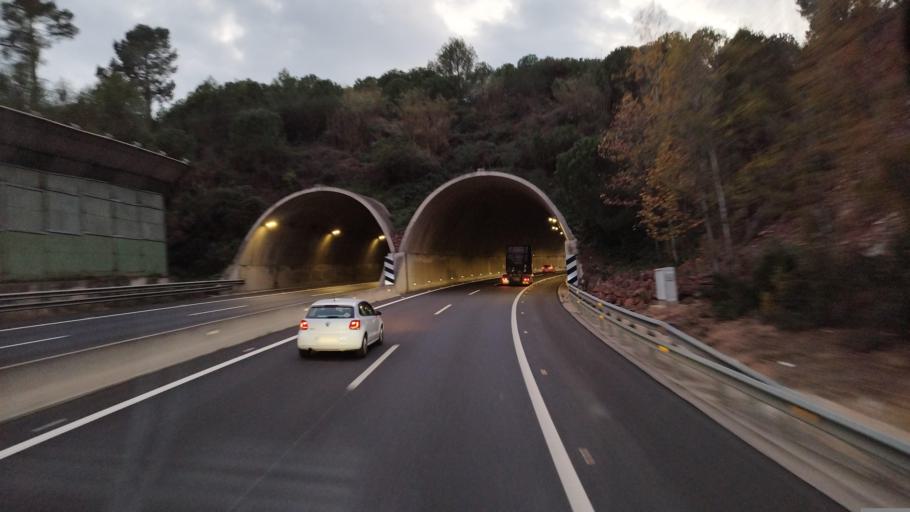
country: ES
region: Catalonia
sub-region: Provincia de Barcelona
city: Cervello
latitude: 41.3915
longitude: 1.9632
